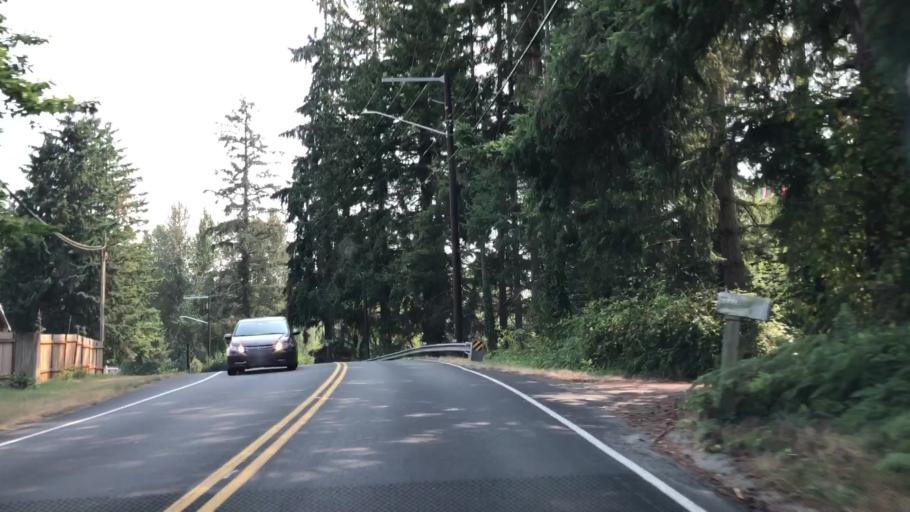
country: US
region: Washington
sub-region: Snohomish County
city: Brier
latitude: 47.7957
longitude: -122.2595
